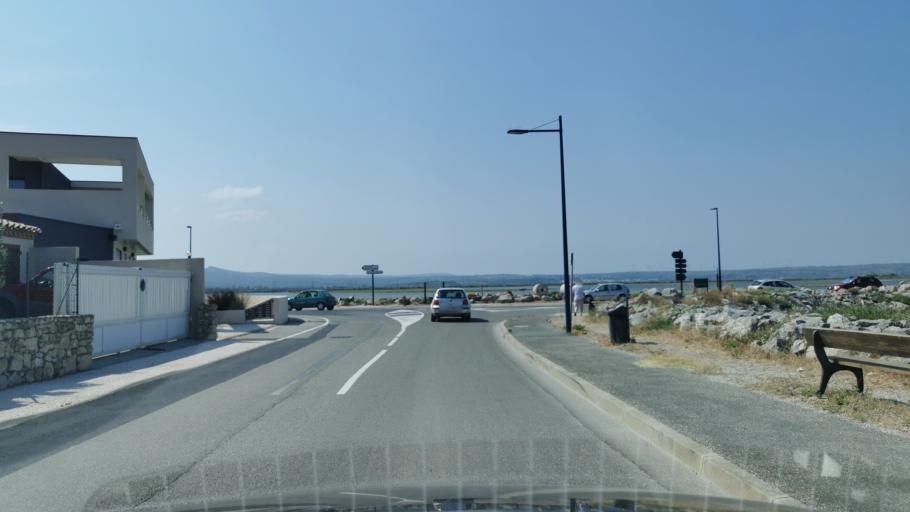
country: FR
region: Languedoc-Roussillon
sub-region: Departement de l'Aude
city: Leucate
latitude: 42.9378
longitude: 3.0266
